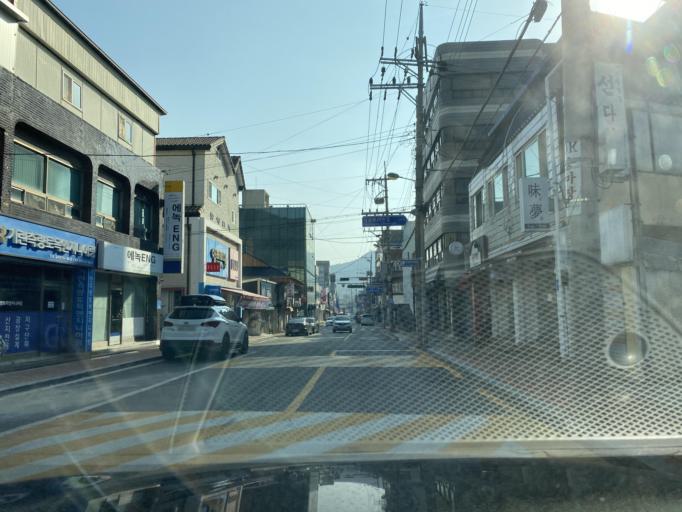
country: KR
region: Chungcheongnam-do
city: Yesan
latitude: 36.6807
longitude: 126.8495
